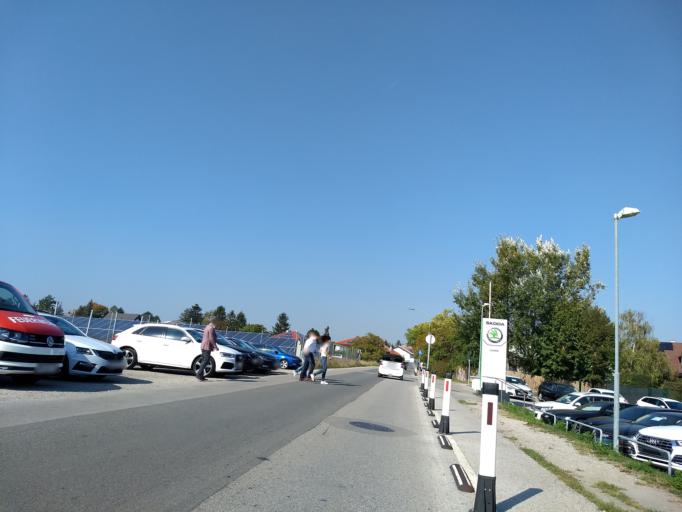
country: AT
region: Lower Austria
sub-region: Politischer Bezirk Modling
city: Brunn am Gebirge
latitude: 48.1159
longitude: 16.2814
